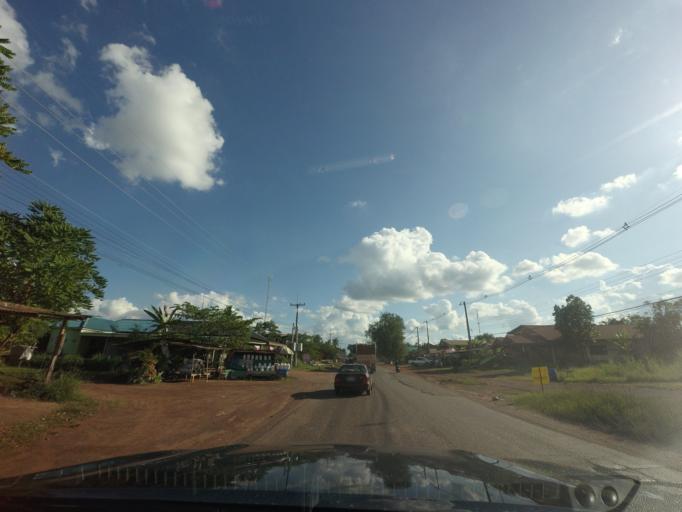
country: TH
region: Changwat Udon Thani
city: Ban Dung
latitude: 17.7348
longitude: 103.2533
